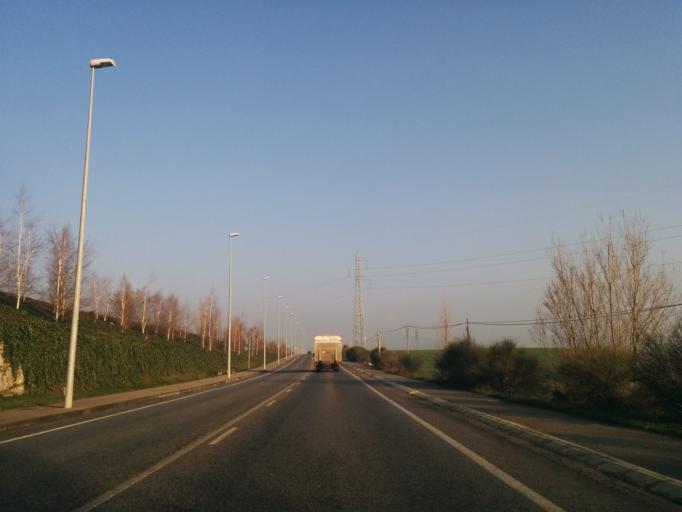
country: ES
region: Navarre
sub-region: Provincia de Navarra
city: Segundo Ensanche
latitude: 42.7751
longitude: -1.6145
